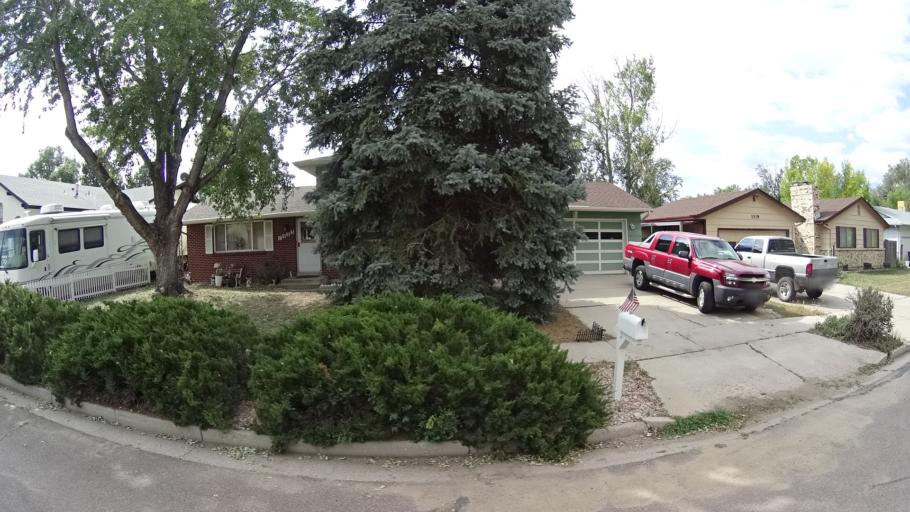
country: US
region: Colorado
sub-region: El Paso County
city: Cimarron Hills
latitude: 38.8549
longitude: -104.7336
